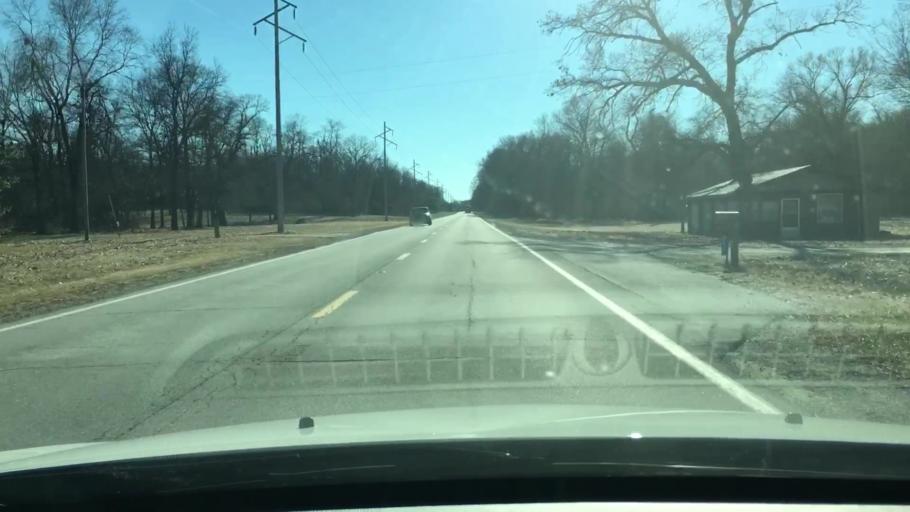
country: US
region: Illinois
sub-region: Morgan County
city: Meredosia
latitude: 39.9093
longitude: -90.4946
